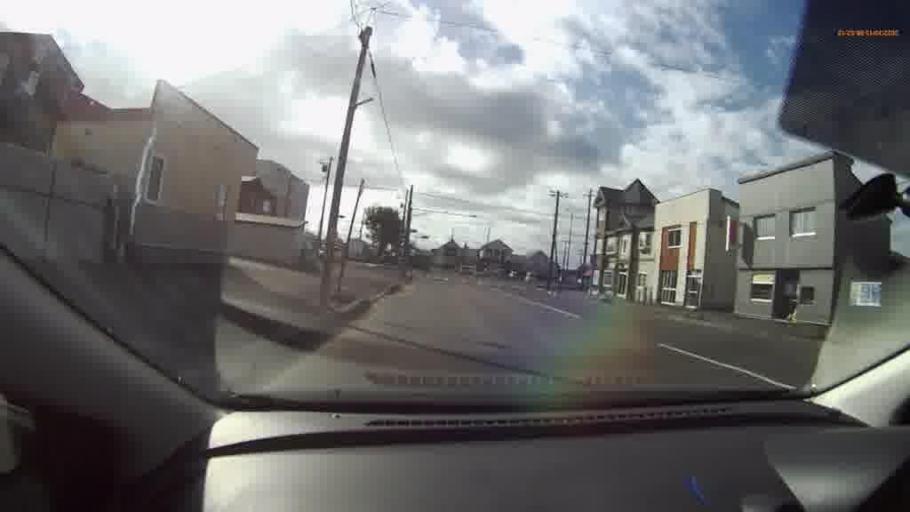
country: JP
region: Hokkaido
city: Kushiro
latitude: 43.0106
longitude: 144.2728
